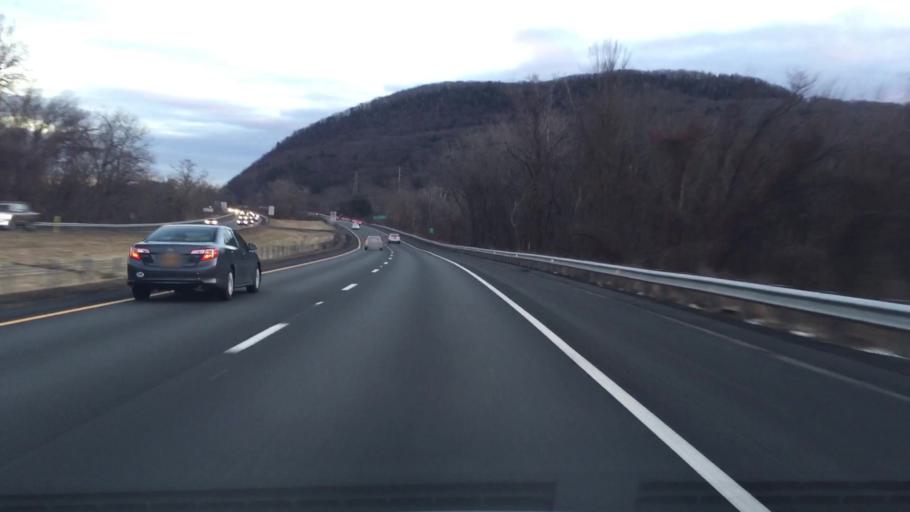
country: US
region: Massachusetts
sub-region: Hampshire County
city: Northampton
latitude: 42.2900
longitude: -72.6264
